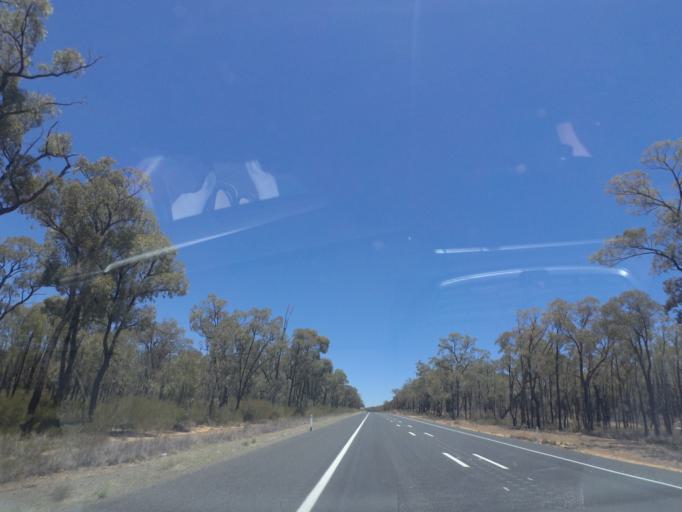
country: AU
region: New South Wales
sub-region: Warrumbungle Shire
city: Coonabarabran
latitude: -30.8827
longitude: 149.4456
